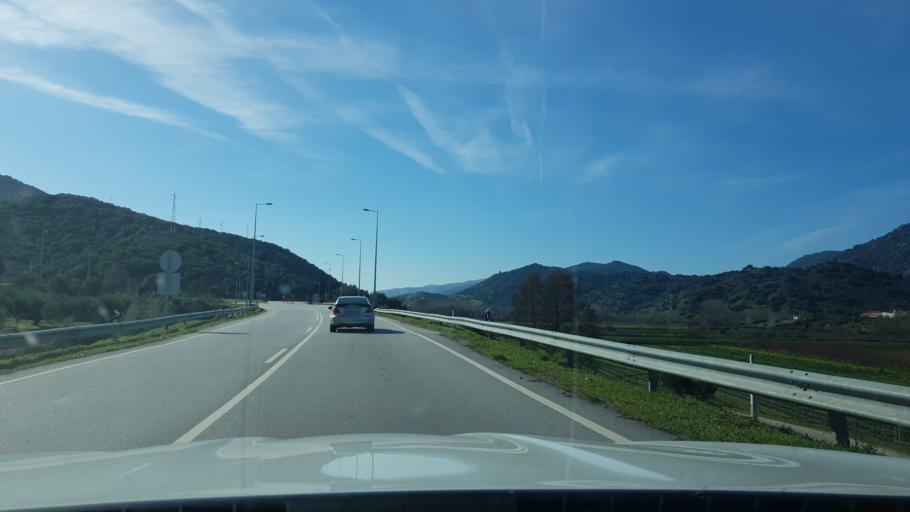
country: PT
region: Braganca
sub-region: Torre de Moncorvo
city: Torre de Moncorvo
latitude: 41.1832
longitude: -7.1024
